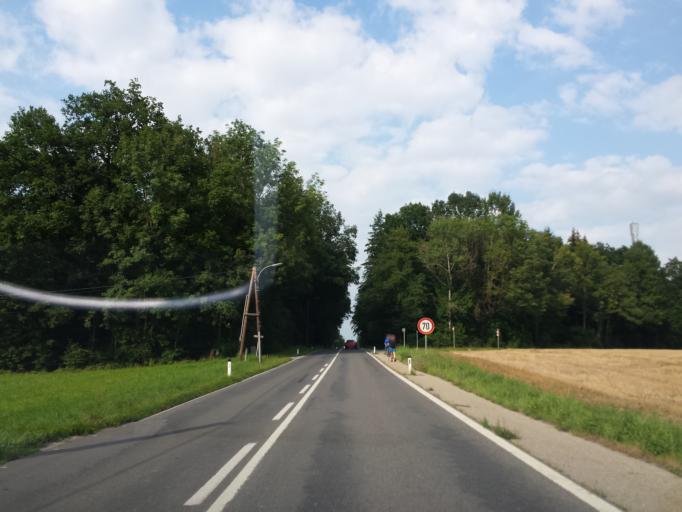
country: AT
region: Styria
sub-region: Politischer Bezirk Graz-Umgebung
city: Pirka
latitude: 46.9921
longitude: 15.3803
